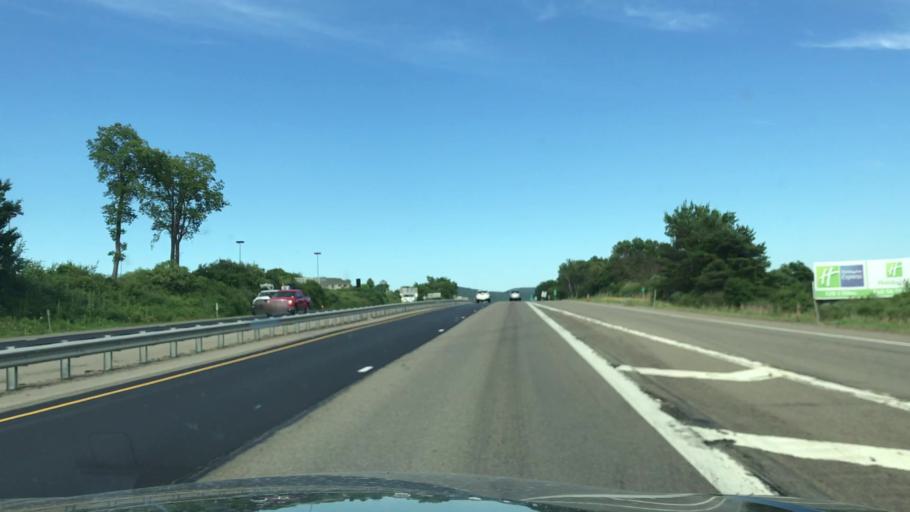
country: US
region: New York
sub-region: Chemung County
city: Horseheads
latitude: 42.1579
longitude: -76.8716
